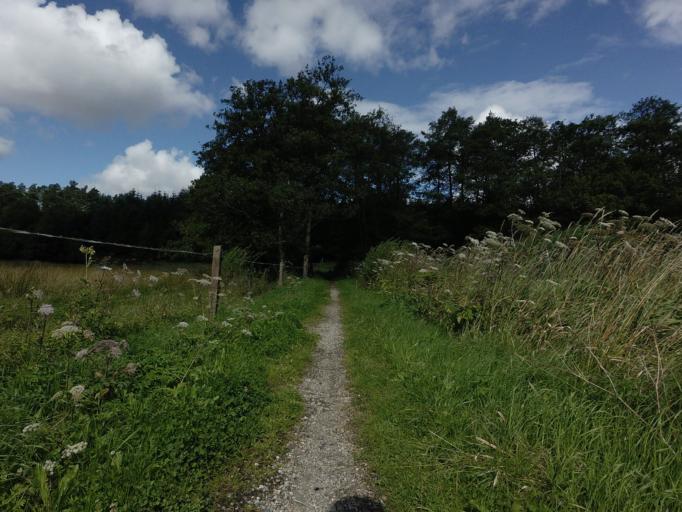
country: DK
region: Central Jutland
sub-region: Silkeborg Kommune
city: Svejbaek
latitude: 56.2186
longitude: 9.7101
